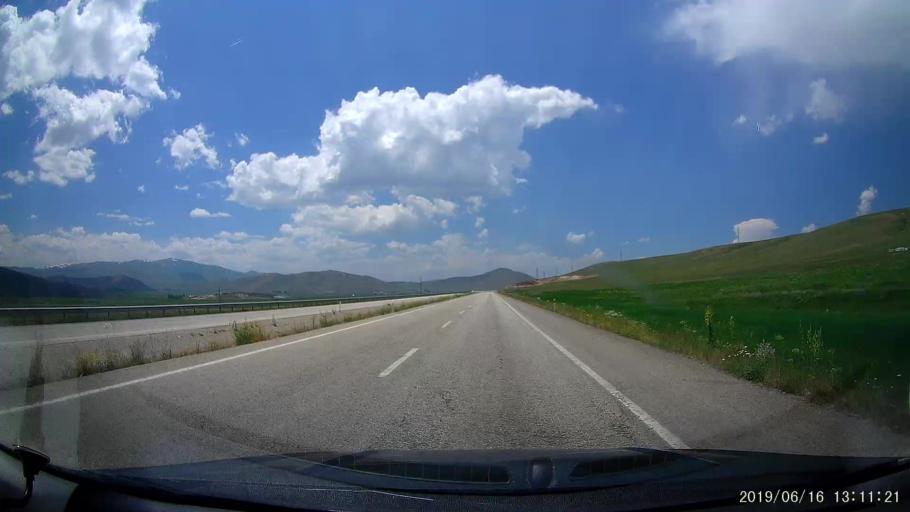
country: TR
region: Agri
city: Diyadin
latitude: 39.5915
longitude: 43.6098
